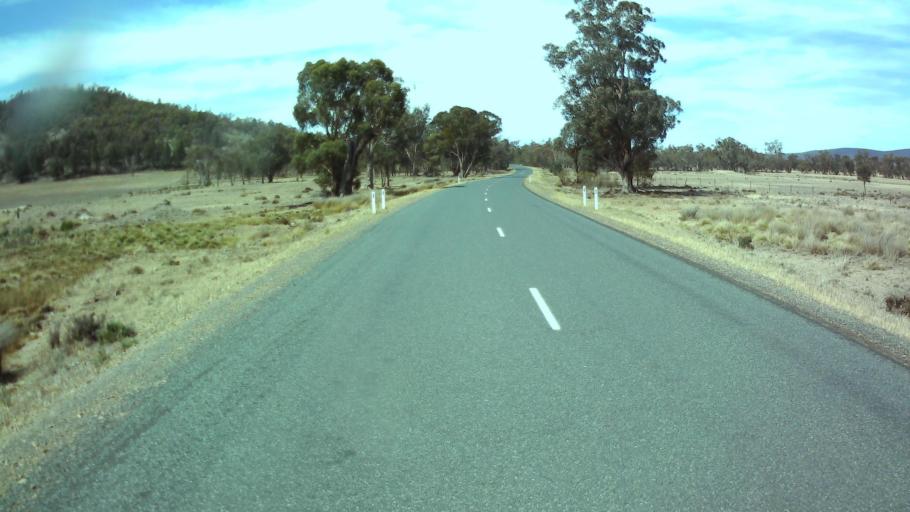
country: AU
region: New South Wales
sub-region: Weddin
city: Grenfell
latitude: -33.6807
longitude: 148.2787
